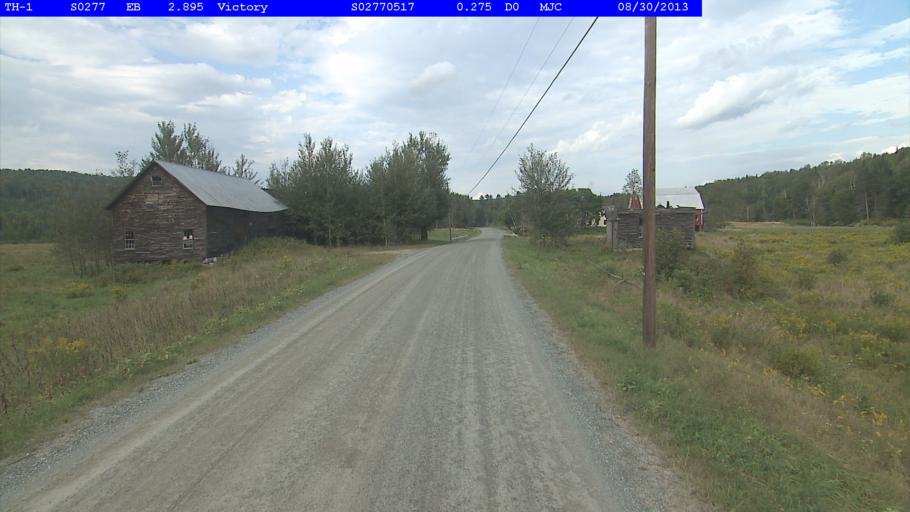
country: US
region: Vermont
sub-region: Caledonia County
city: Lyndonville
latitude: 44.5001
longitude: -71.8532
